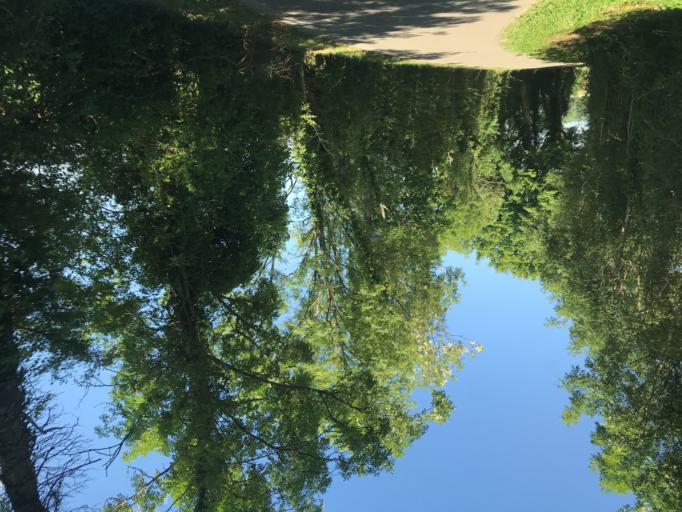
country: FR
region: Rhone-Alpes
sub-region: Departement de l'Ain
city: Tramoyes
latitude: 45.8801
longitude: 4.9645
